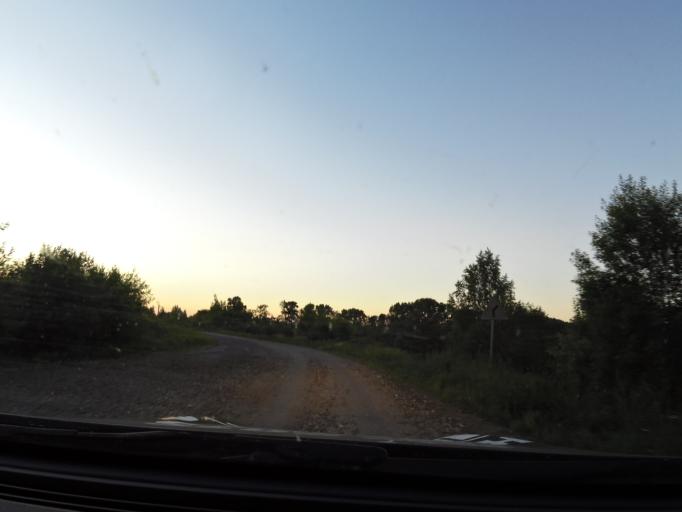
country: RU
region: Kostroma
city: Buy
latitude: 58.4056
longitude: 41.2417
